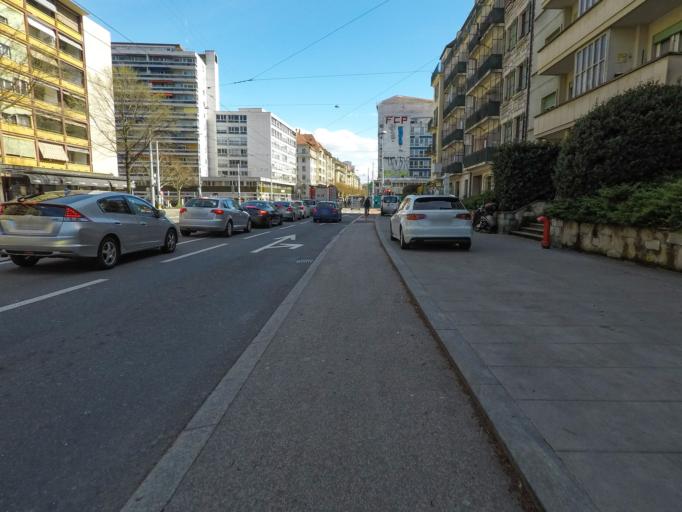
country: CH
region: Geneva
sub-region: Geneva
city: Le Grand-Saconnex
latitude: 46.2140
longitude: 6.1286
